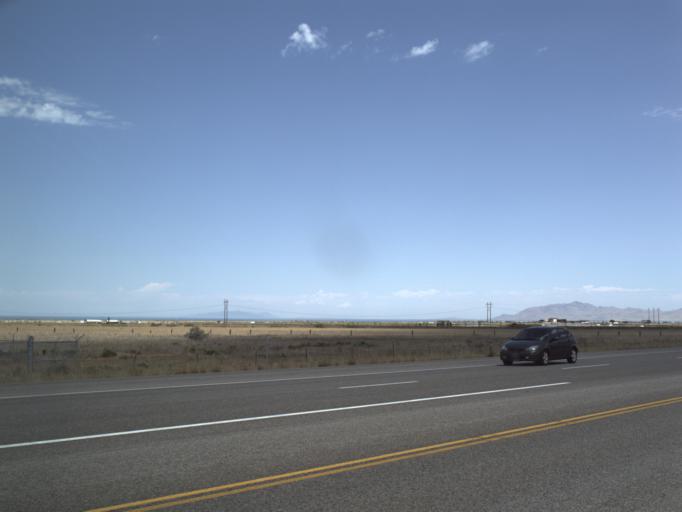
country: US
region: Utah
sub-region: Tooele County
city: Stansbury park
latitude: 40.6662
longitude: -112.2854
